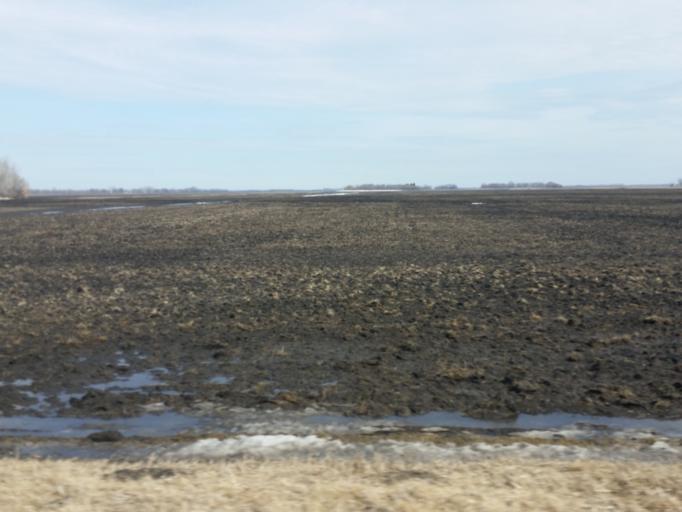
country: US
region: North Dakota
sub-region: Walsh County
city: Grafton
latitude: 48.4287
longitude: -97.2558
